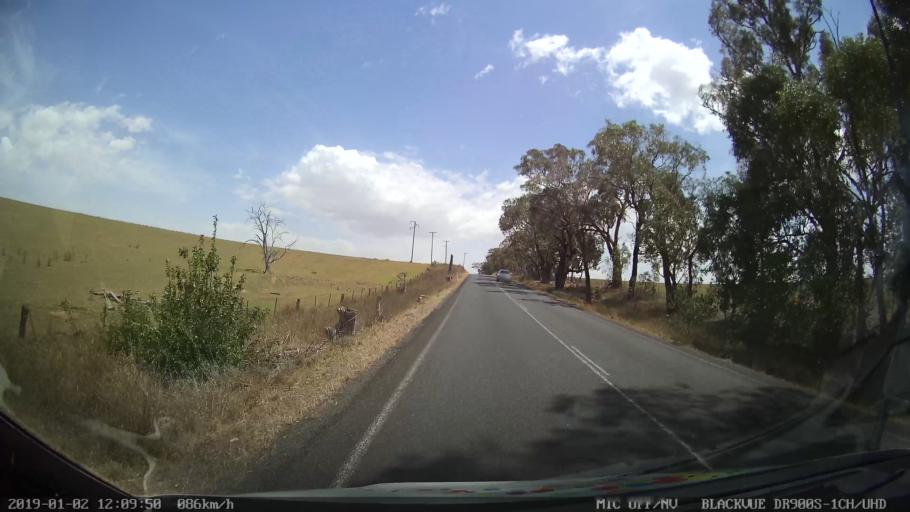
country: AU
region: New South Wales
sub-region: Young
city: Young
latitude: -34.4672
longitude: 148.2675
